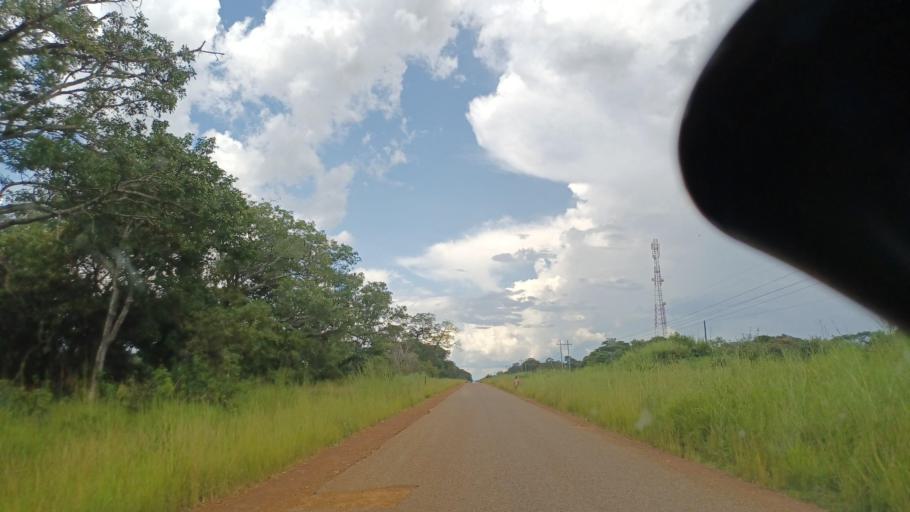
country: ZM
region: North-Western
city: Kasempa
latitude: -12.7940
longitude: 26.0155
